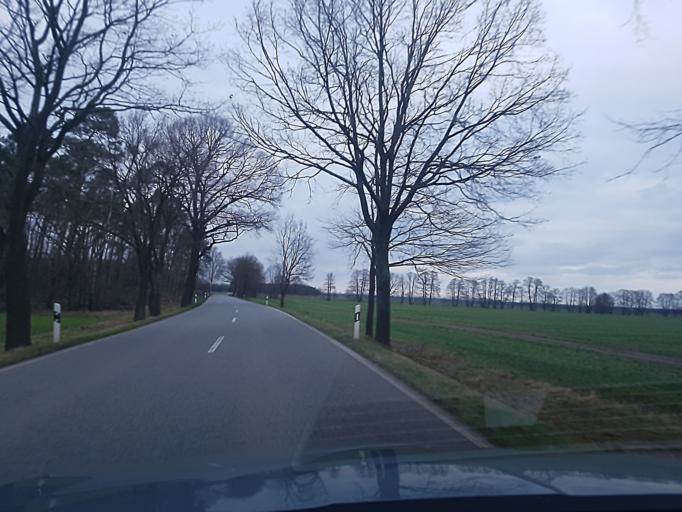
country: DE
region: Brandenburg
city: Finsterwalde
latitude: 51.6667
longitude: 13.6922
